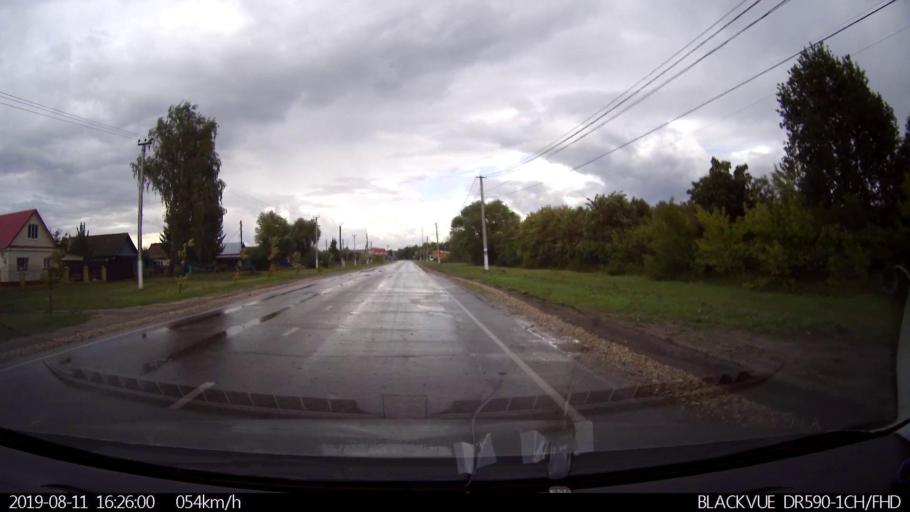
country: RU
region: Ulyanovsk
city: Mayna
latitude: 54.1084
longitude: 47.6114
